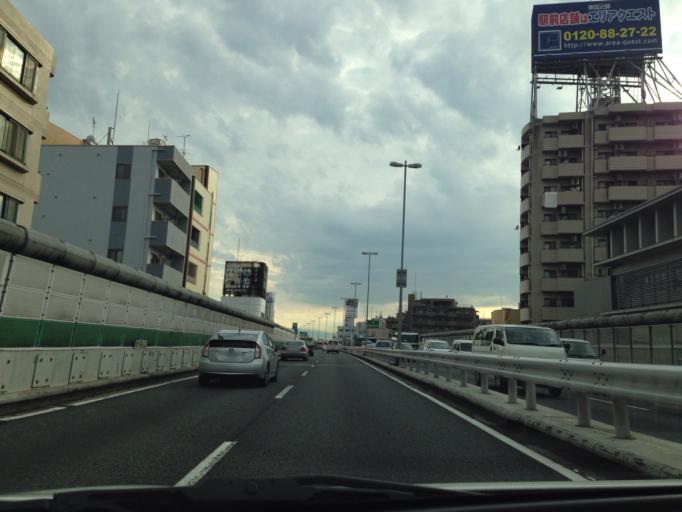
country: JP
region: Tokyo
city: Tokyo
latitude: 35.6307
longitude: 139.6550
